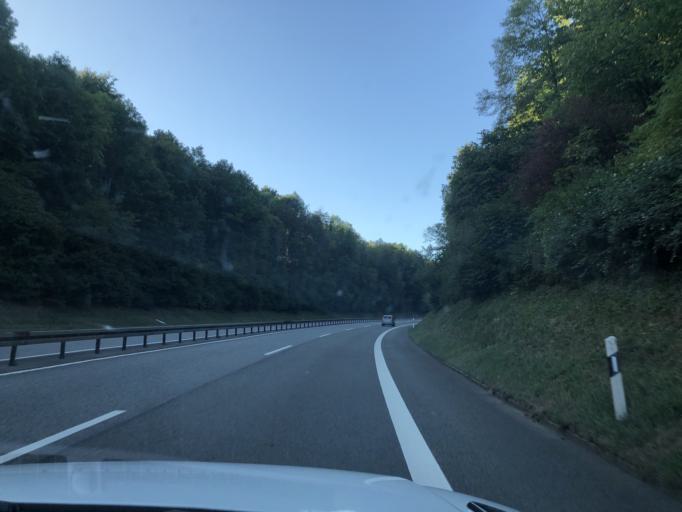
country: DE
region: Saarland
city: Illingen
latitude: 49.3928
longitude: 7.0113
